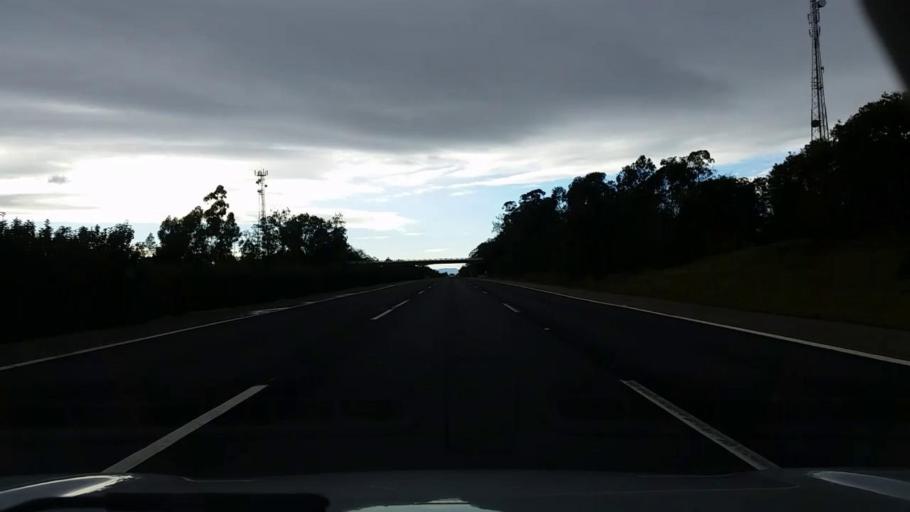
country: BR
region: Rio Grande do Sul
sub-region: Taquara
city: Taquara
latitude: -29.8904
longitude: -50.7072
